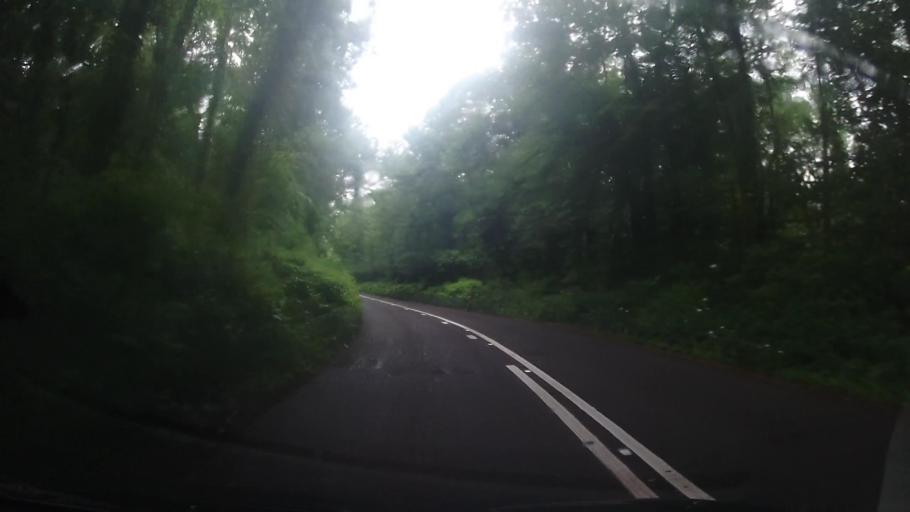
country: GB
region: England
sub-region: Devon
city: Dartmouth
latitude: 50.3768
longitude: -3.5501
